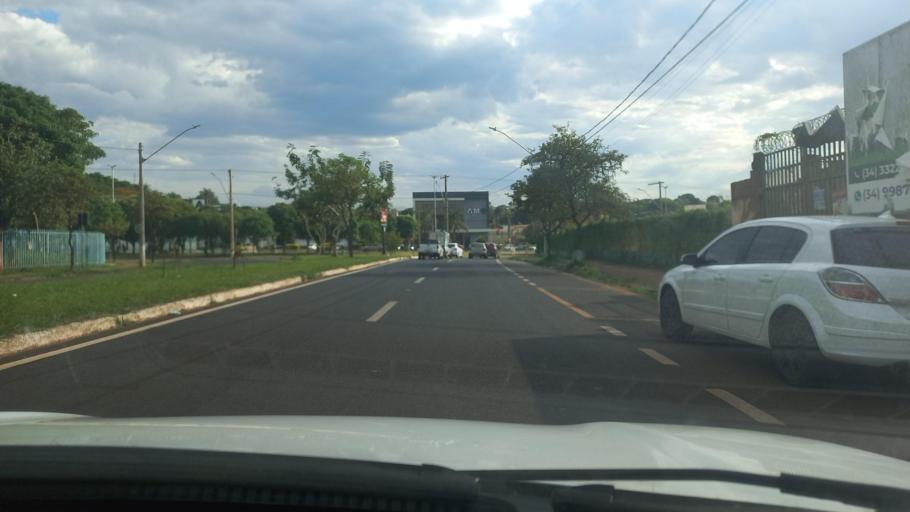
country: BR
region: Minas Gerais
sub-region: Uberaba
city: Uberaba
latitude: -19.7544
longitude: -47.9157
